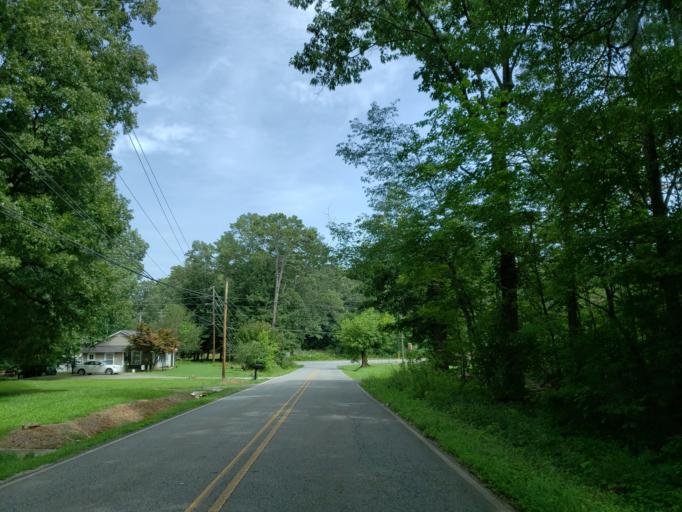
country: US
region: Georgia
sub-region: Pickens County
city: Nelson
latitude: 34.3661
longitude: -84.3761
